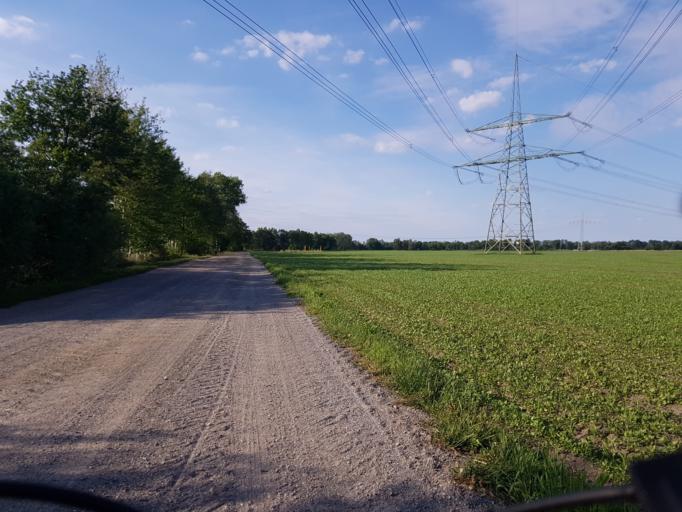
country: DE
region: Brandenburg
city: Merzdorf
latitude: 51.4242
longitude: 13.5266
